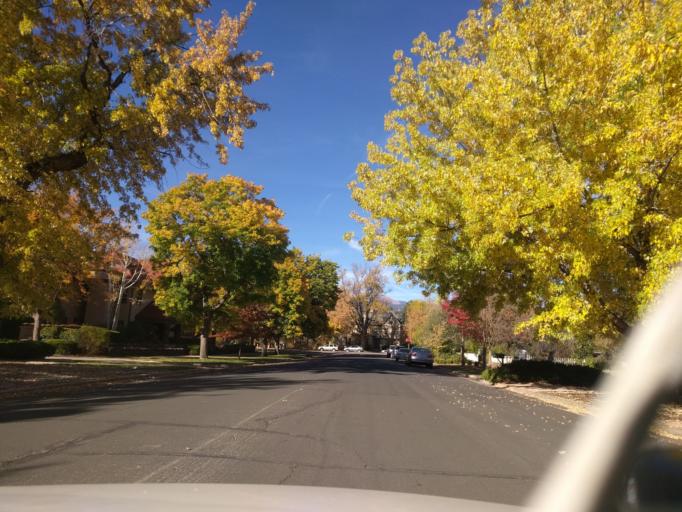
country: US
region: Colorado
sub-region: El Paso County
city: Colorado Springs
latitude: 38.8524
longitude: -104.8250
